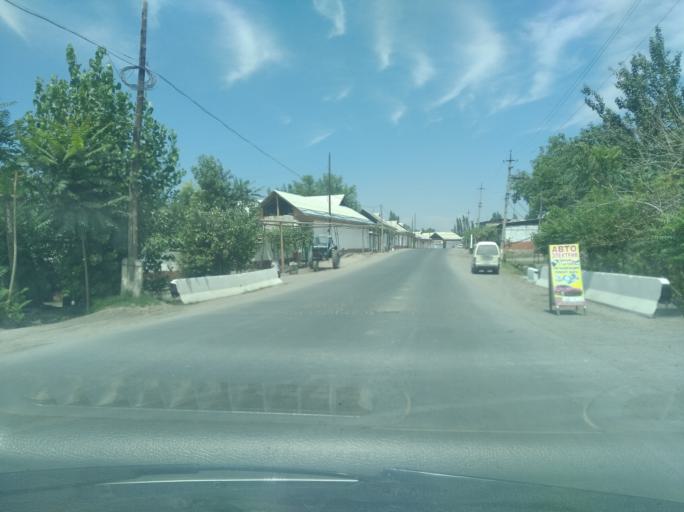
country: KG
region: Osh
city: Aravan
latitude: 40.6228
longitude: 72.4508
